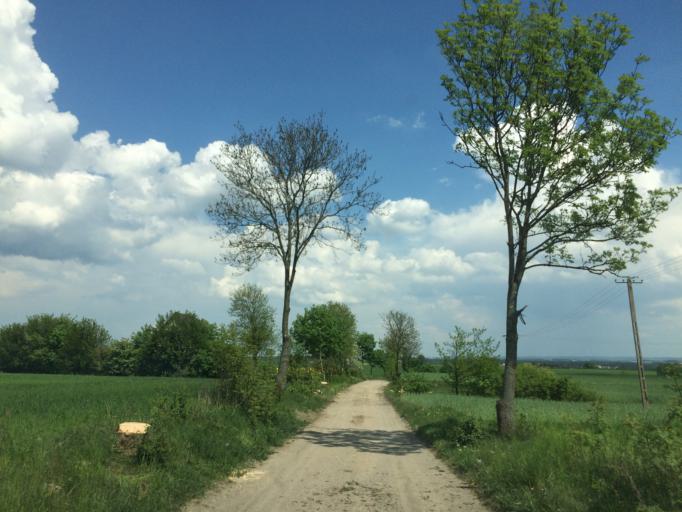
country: PL
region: Warmian-Masurian Voivodeship
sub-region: Powiat nowomiejski
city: Nowe Miasto Lubawskie
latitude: 53.4496
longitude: 19.5772
